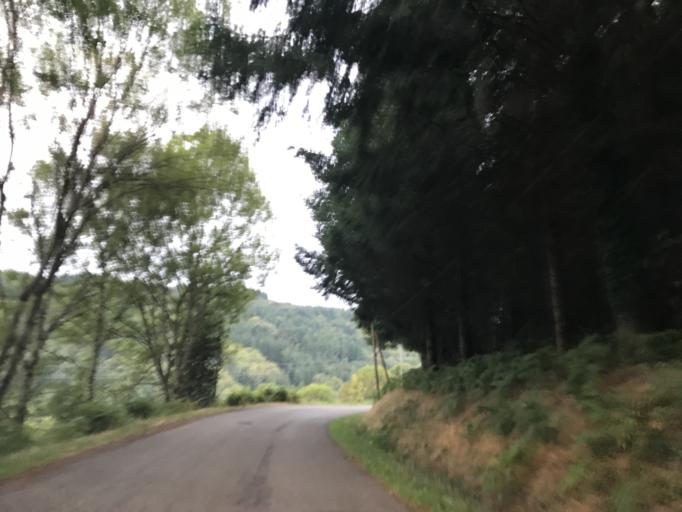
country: FR
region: Auvergne
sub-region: Departement du Puy-de-Dome
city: Thiers
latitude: 45.8513
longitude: 3.5822
